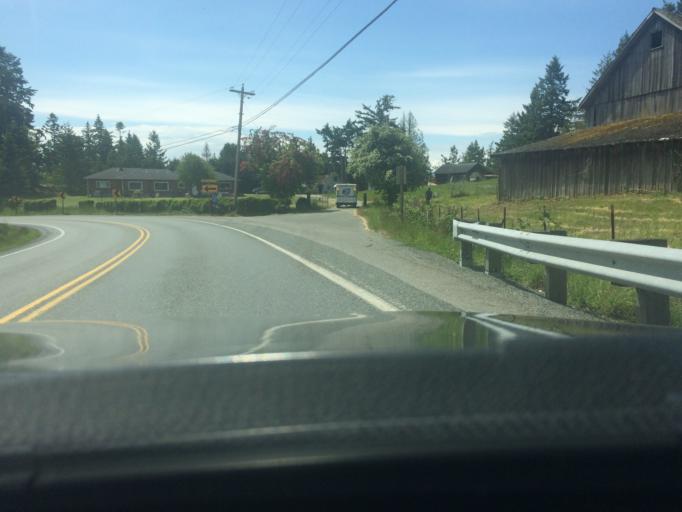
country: US
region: Washington
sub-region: Island County
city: Ault Field
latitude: 48.4239
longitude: -122.6653
